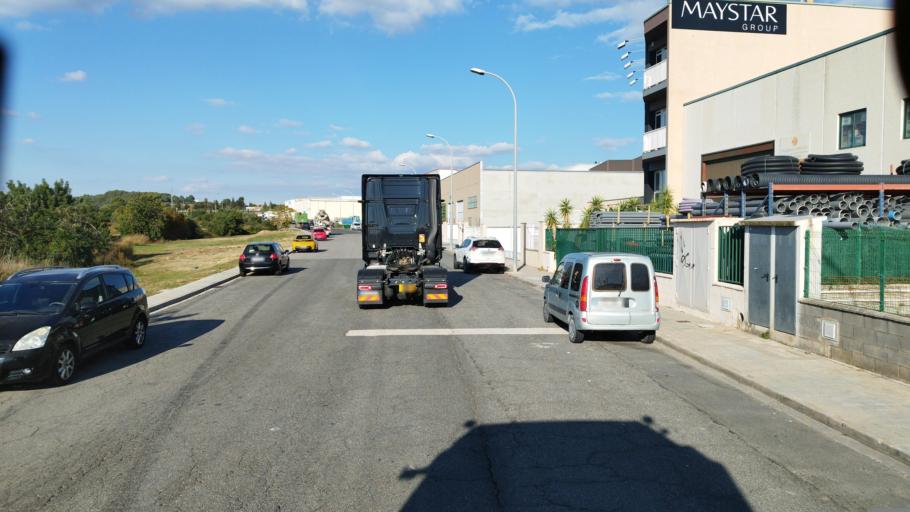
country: ES
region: Catalonia
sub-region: Provincia de Tarragona
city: Torredembarra
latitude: 41.1537
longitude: 1.3907
